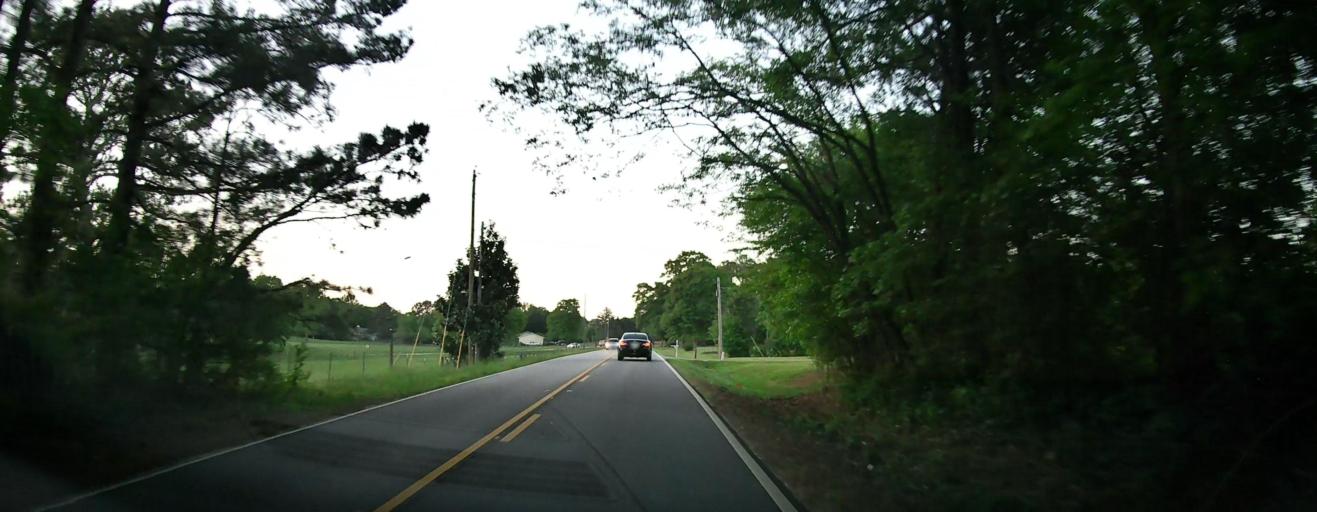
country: US
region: Georgia
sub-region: Henry County
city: McDonough
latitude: 33.4722
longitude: -84.1944
